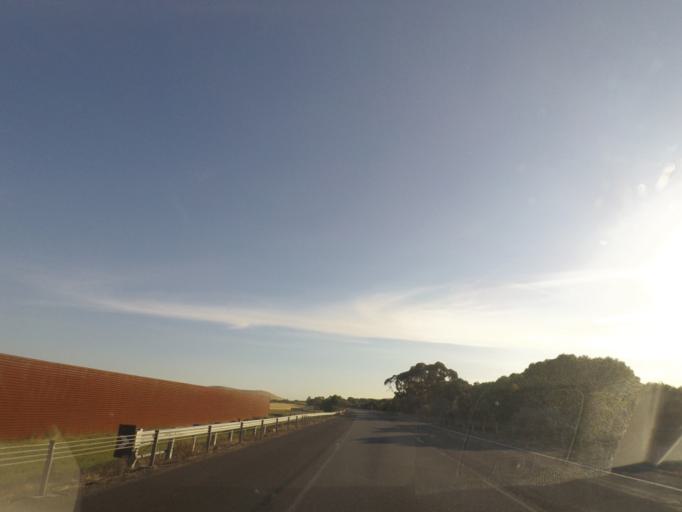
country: AU
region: Victoria
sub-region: Whittlesea
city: Whittlesea
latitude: -37.4297
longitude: 144.9843
